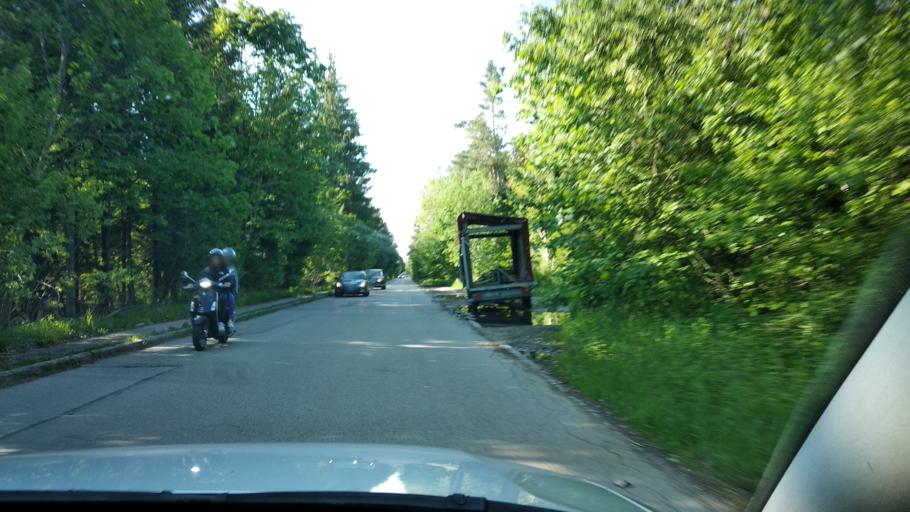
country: DE
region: Bavaria
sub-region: Upper Bavaria
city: Ottobrunn
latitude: 48.0446
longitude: 11.6652
